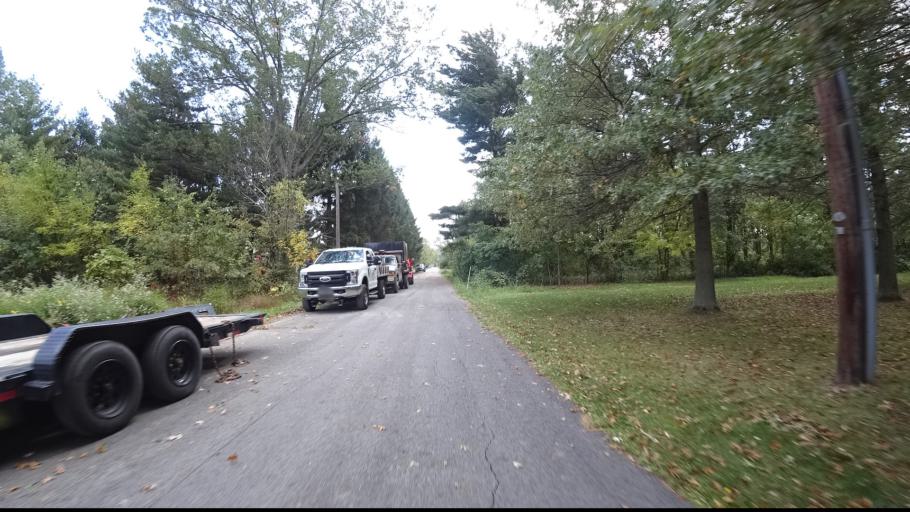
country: US
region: Indiana
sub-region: Porter County
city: Burns Harbor
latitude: 41.6141
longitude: -87.1159
